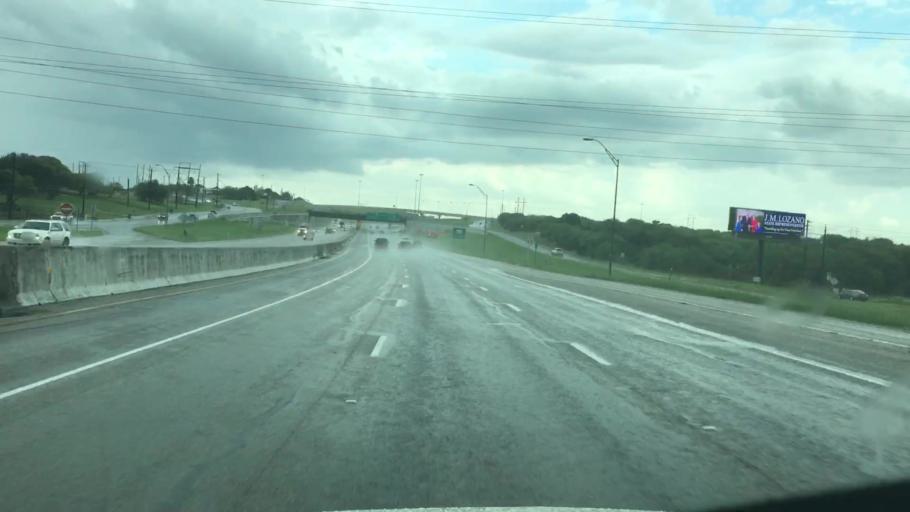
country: US
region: Texas
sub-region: Nueces County
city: Robstown
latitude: 27.8607
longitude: -97.6124
